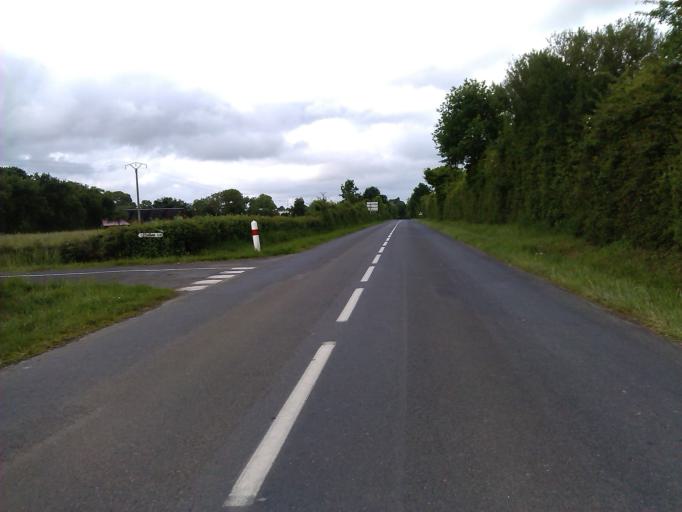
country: FR
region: Poitou-Charentes
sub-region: Departement de la Vienne
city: Availles-Limouzine
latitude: 46.1958
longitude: 0.6415
